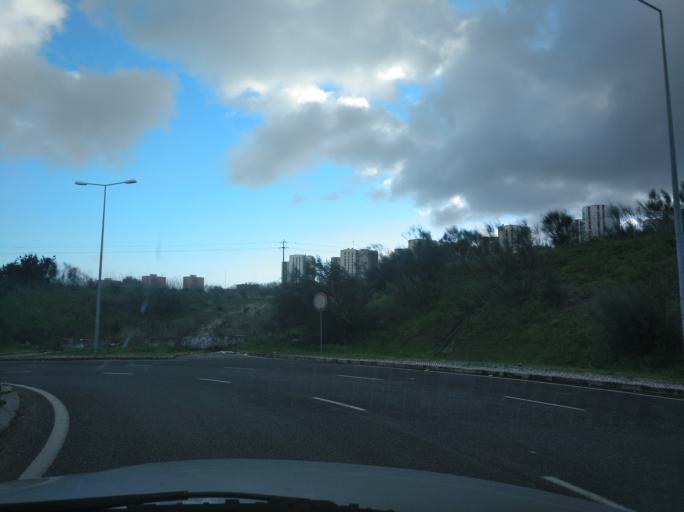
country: PT
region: Lisbon
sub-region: Loures
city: Loures
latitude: 38.8169
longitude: -9.1780
